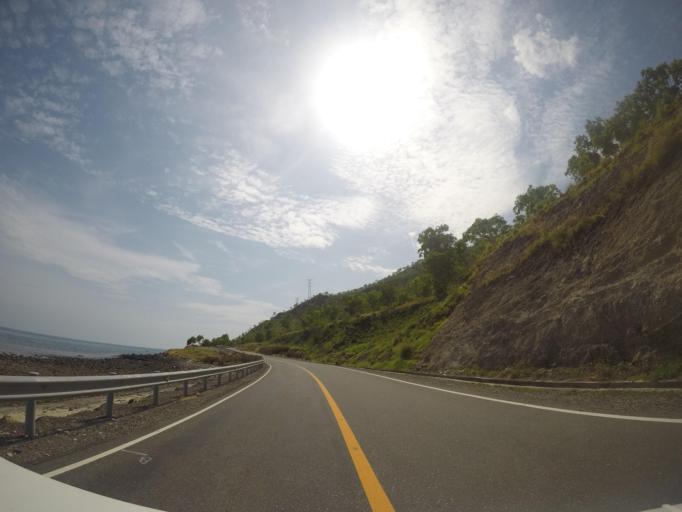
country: TL
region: Manatuto
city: Manatuto
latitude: -8.4789
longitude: 125.9349
